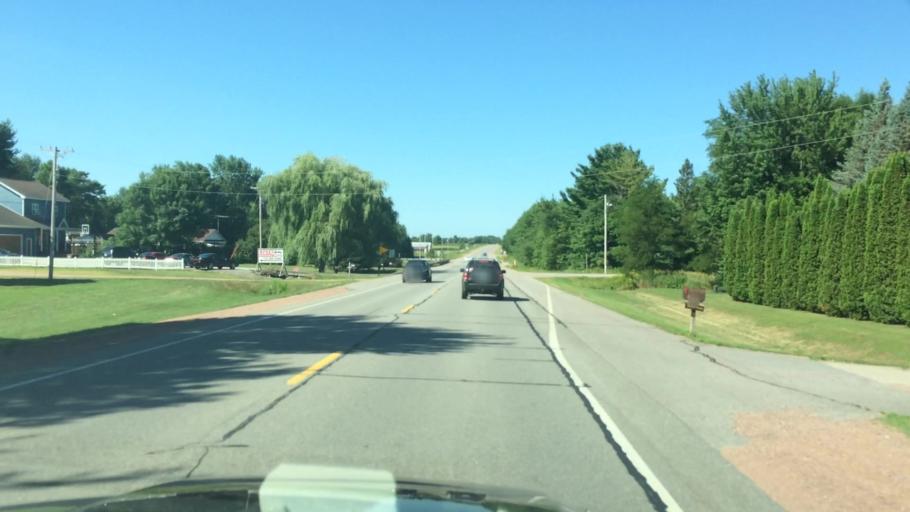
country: US
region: Wisconsin
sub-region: Marathon County
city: Stratford
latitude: 44.7231
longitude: -90.0977
